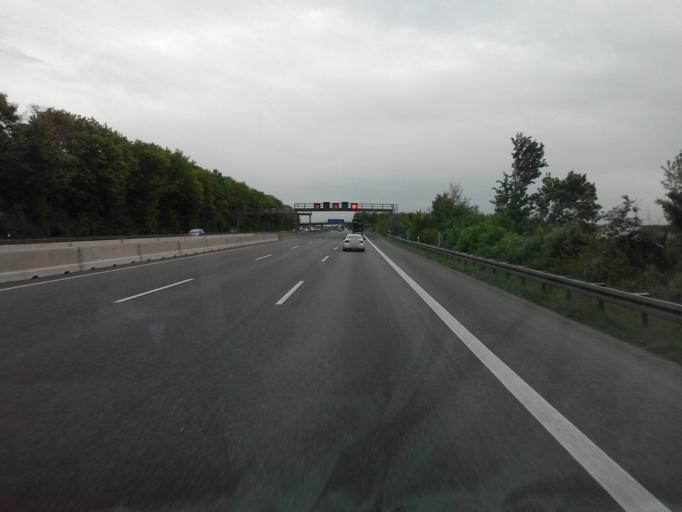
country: DE
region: North Rhine-Westphalia
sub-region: Regierungsbezirk Koln
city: Weilerswist
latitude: 50.7823
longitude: 6.8104
